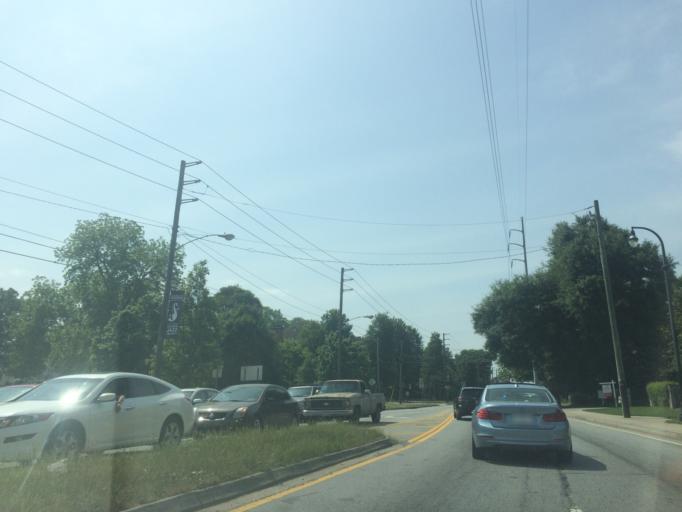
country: US
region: Georgia
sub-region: DeKalb County
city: Druid Hills
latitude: 33.7699
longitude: -84.3491
